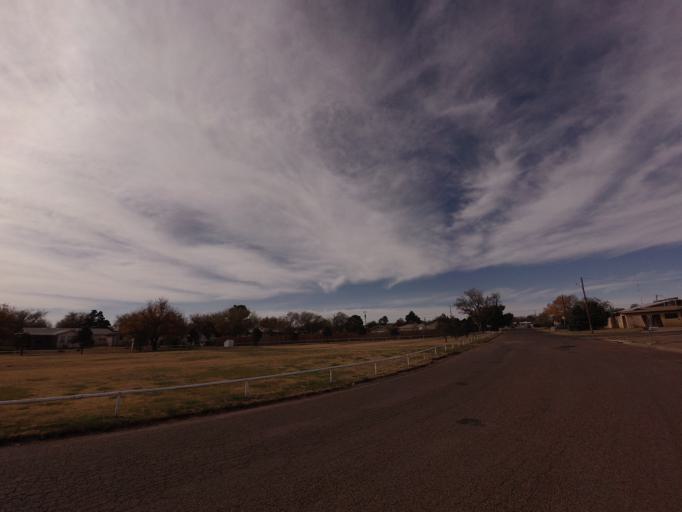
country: US
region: New Mexico
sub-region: Curry County
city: Clovis
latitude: 34.4130
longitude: -103.1935
